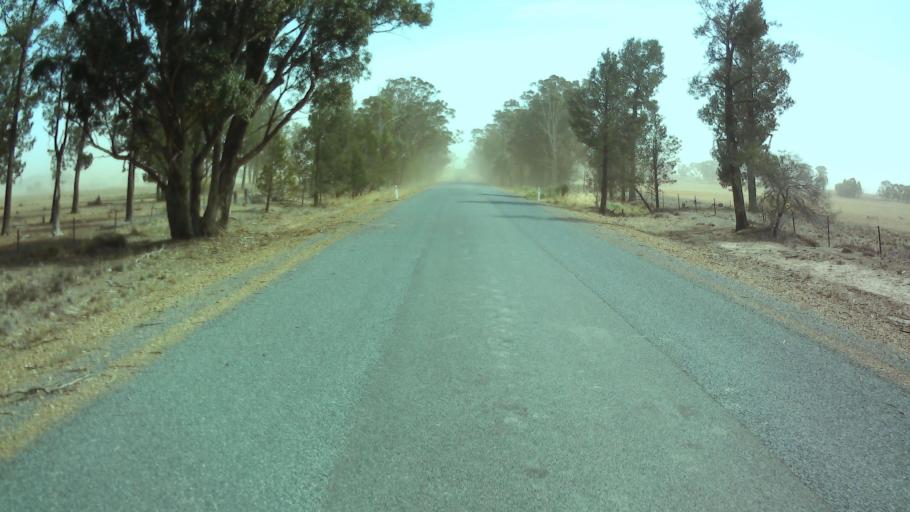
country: AU
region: New South Wales
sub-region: Weddin
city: Grenfell
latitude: -33.7540
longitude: 147.9901
